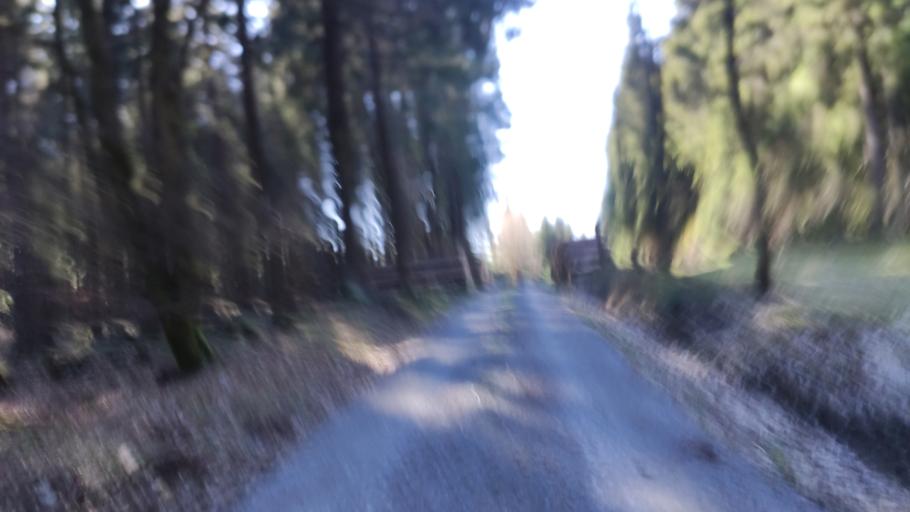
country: DE
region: Bavaria
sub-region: Upper Franconia
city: Reichenbach
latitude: 50.4417
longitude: 11.4429
